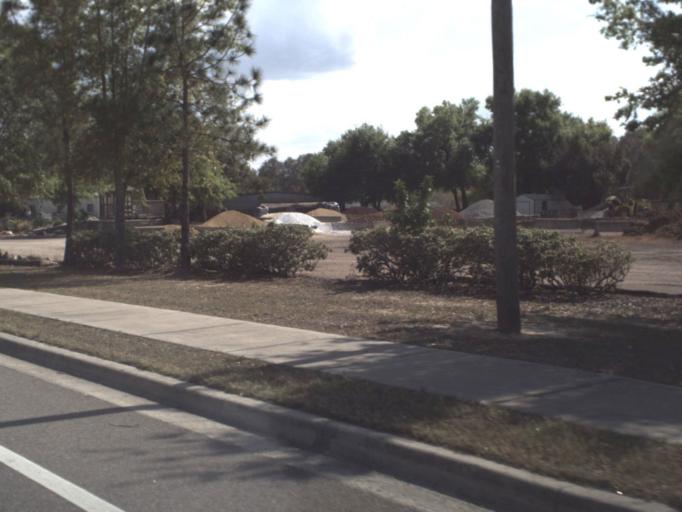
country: US
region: Florida
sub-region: Lake County
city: Minneola
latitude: 28.5772
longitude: -81.7494
